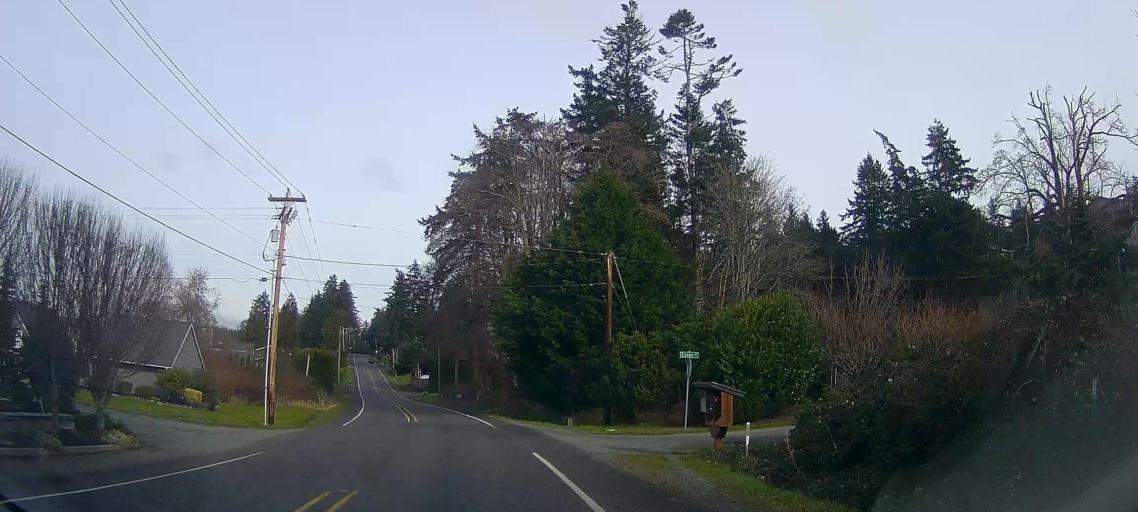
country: US
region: Washington
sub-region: Island County
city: Camano
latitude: 48.2505
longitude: -122.4797
